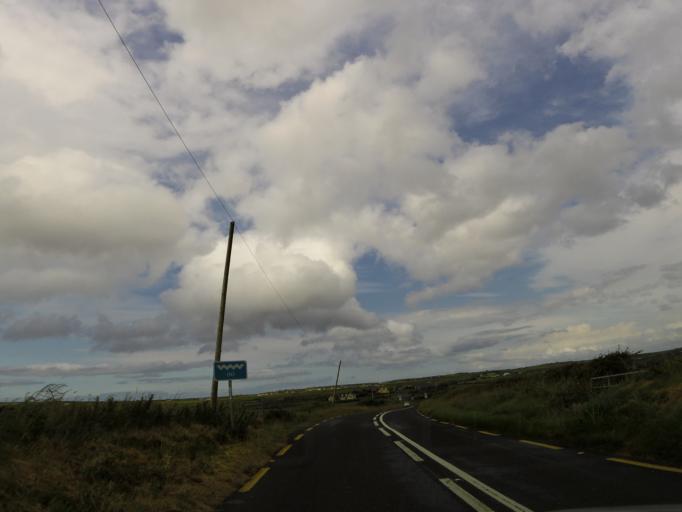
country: IE
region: Munster
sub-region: An Clar
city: Kilrush
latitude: 52.7094
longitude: -9.5922
